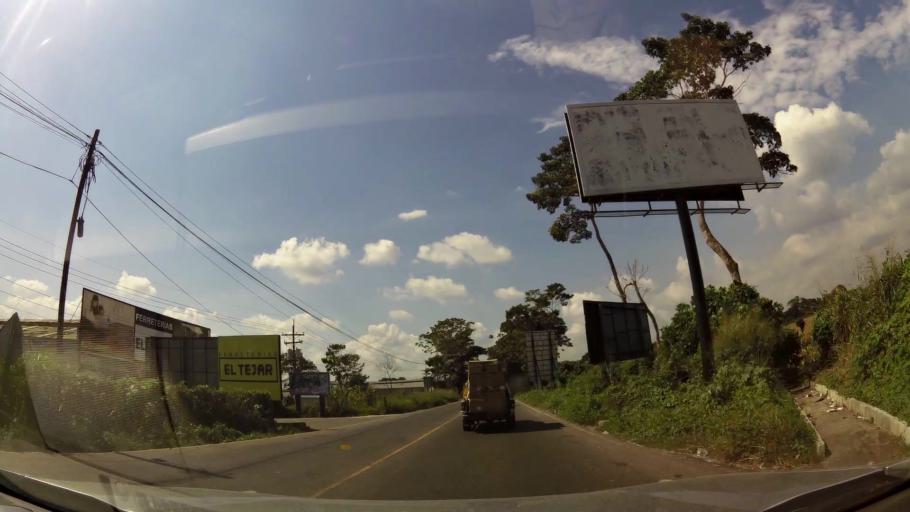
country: GT
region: Suchitepeque
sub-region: Municipio de San Gabriel
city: San Gabriel
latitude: 14.5354
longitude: -91.5253
